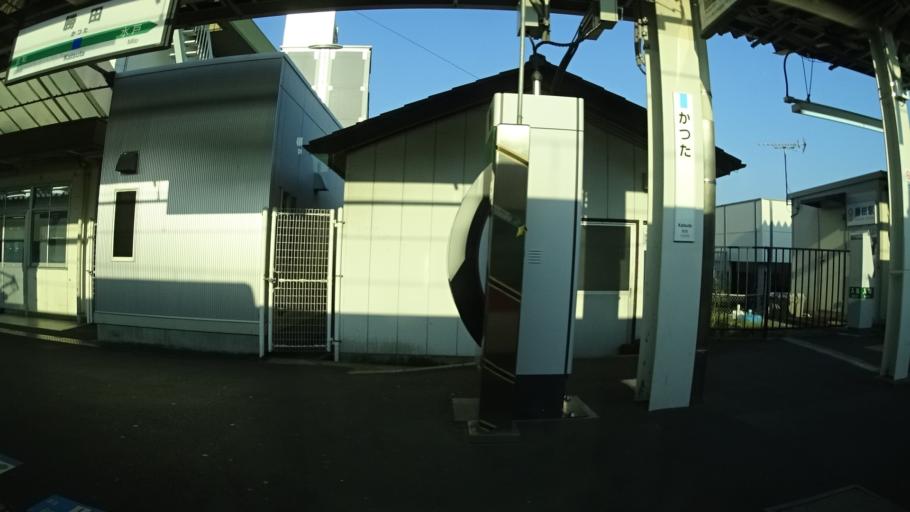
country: JP
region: Ibaraki
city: Hitachi-Naka
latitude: 36.3938
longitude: 140.5242
